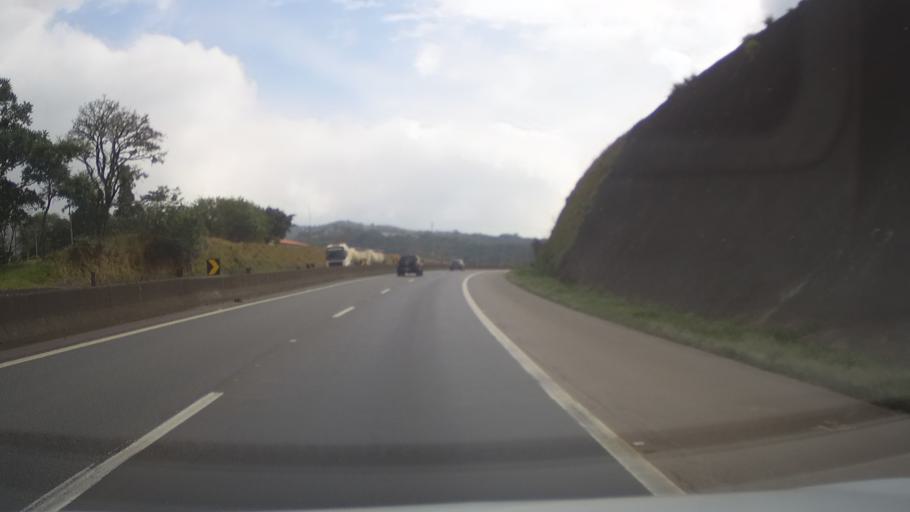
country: BR
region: Minas Gerais
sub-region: Extrema
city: Extrema
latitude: -22.8854
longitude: -46.4107
